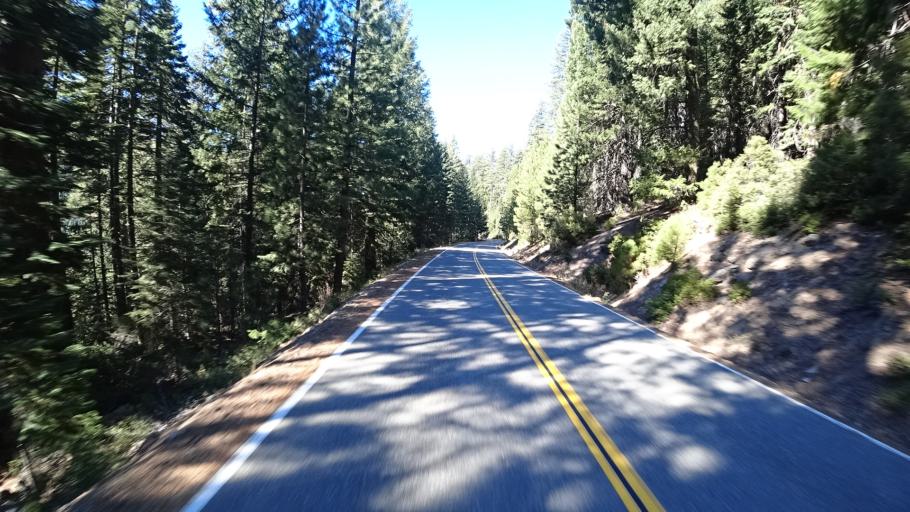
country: US
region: California
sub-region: Trinity County
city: Weaverville
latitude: 41.2288
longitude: -122.9504
